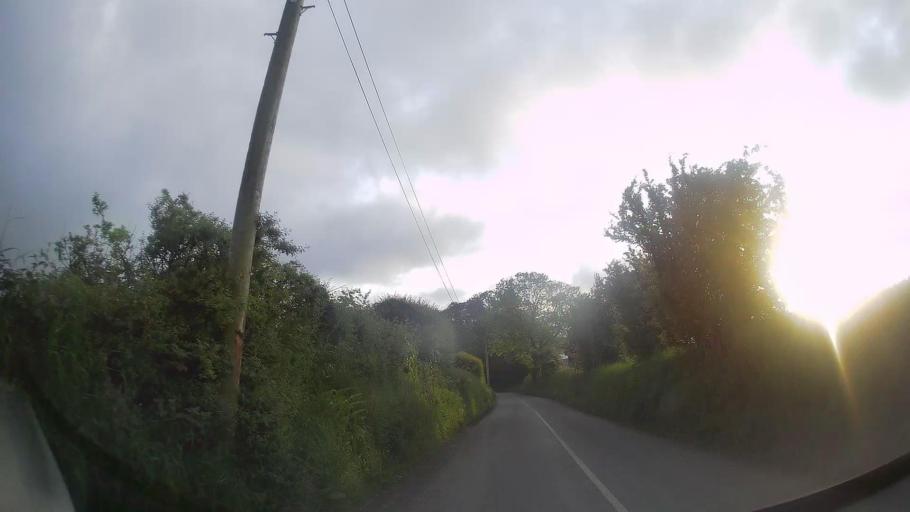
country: IE
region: Munster
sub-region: County Cork
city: Blarney
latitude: 51.9785
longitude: -8.5486
